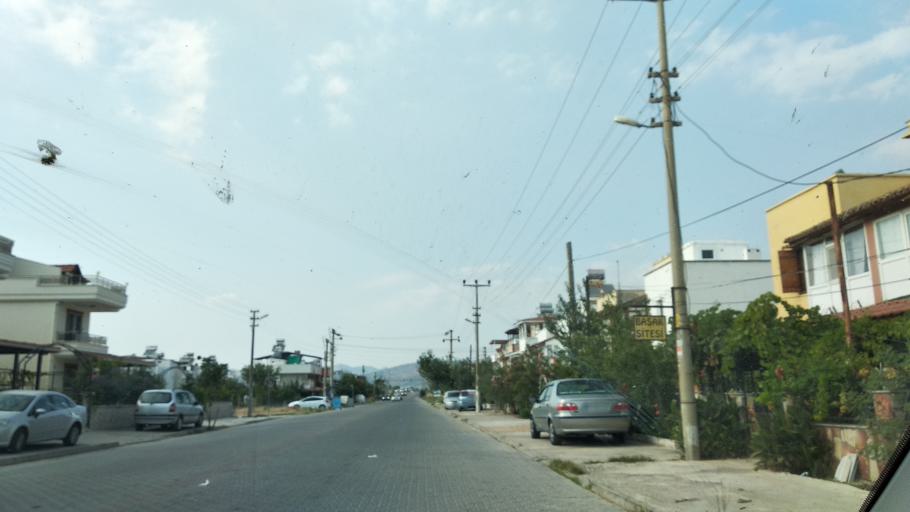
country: TR
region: Izmir
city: Dikili
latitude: 39.1012
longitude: 26.8828
